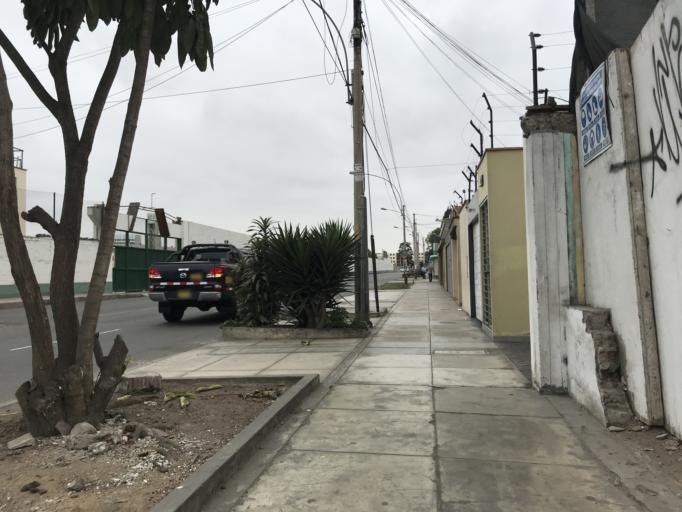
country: PE
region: Callao
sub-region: Callao
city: Callao
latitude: -12.0743
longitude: -77.0761
